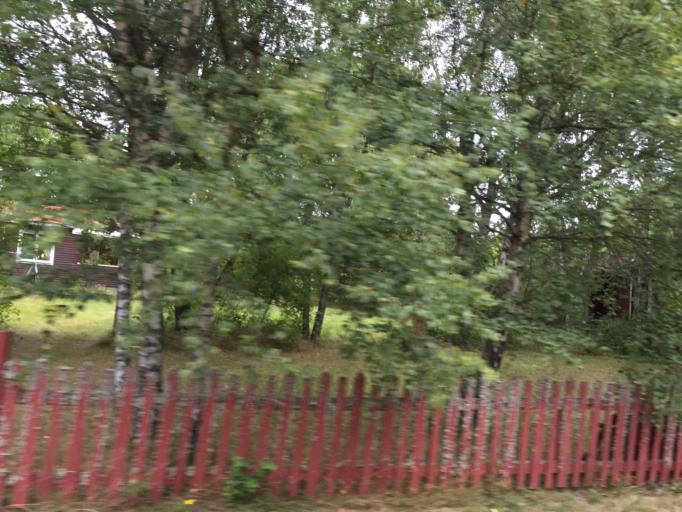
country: SE
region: Kalmar
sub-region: Monsteras Kommun
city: Moensteras
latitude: 57.0463
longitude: 16.5745
